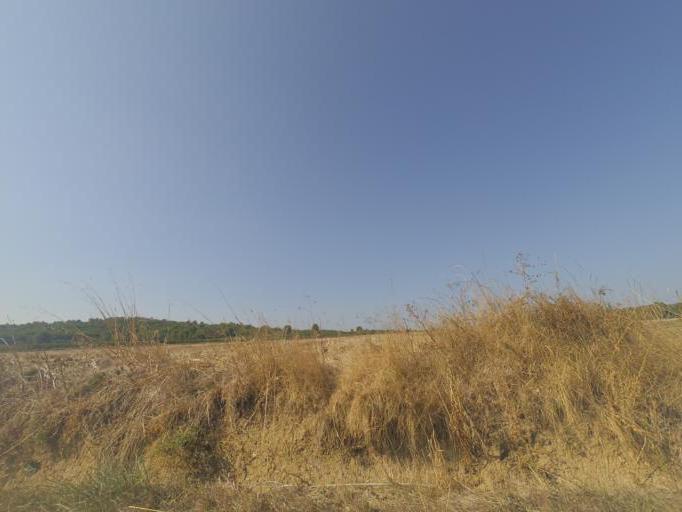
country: FR
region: Languedoc-Roussillon
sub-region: Departement du Gard
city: Calvisson
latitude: 43.7661
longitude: 4.1913
